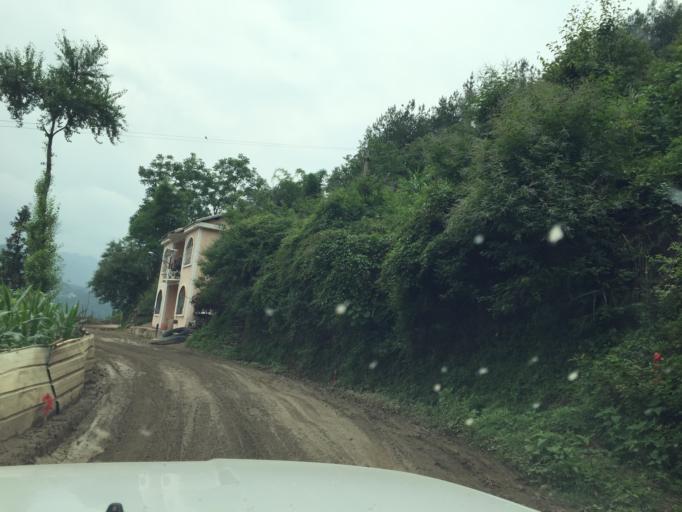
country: CN
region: Guizhou Sheng
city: Tongjing
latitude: 28.3713
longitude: 108.2404
